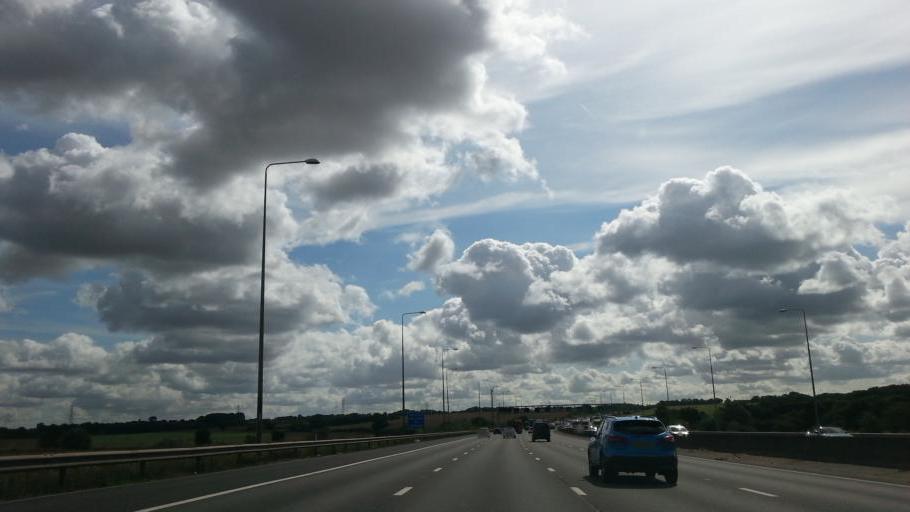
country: GB
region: England
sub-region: Greater London
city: Collier Row
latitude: 51.6548
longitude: 0.1864
